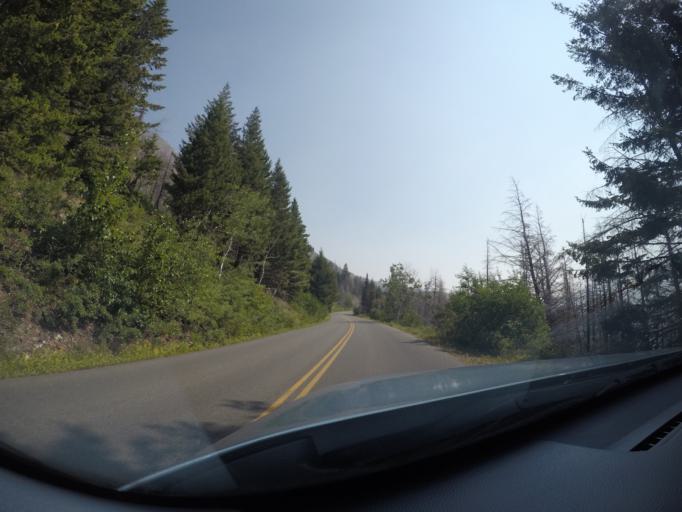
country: US
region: Montana
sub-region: Glacier County
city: Browning
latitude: 48.6925
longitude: -113.5529
